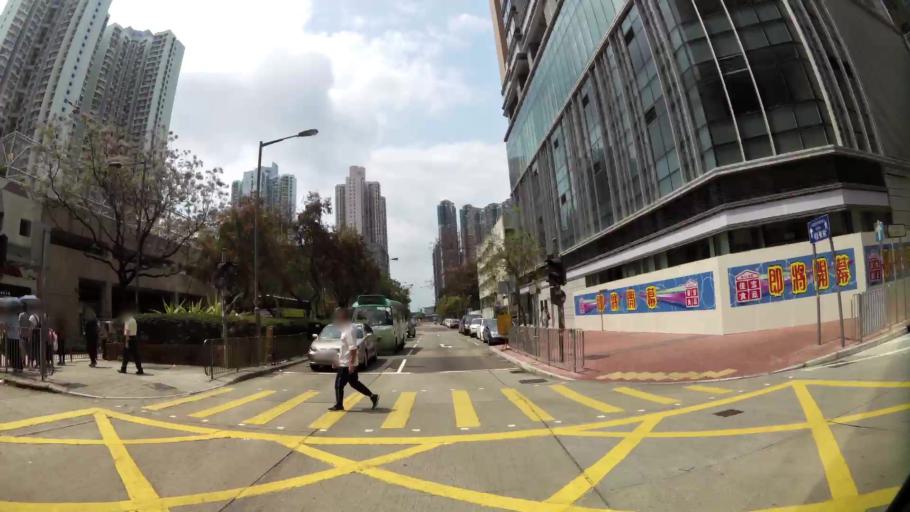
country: HK
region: Sham Shui Po
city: Sham Shui Po
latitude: 22.3389
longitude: 114.1548
